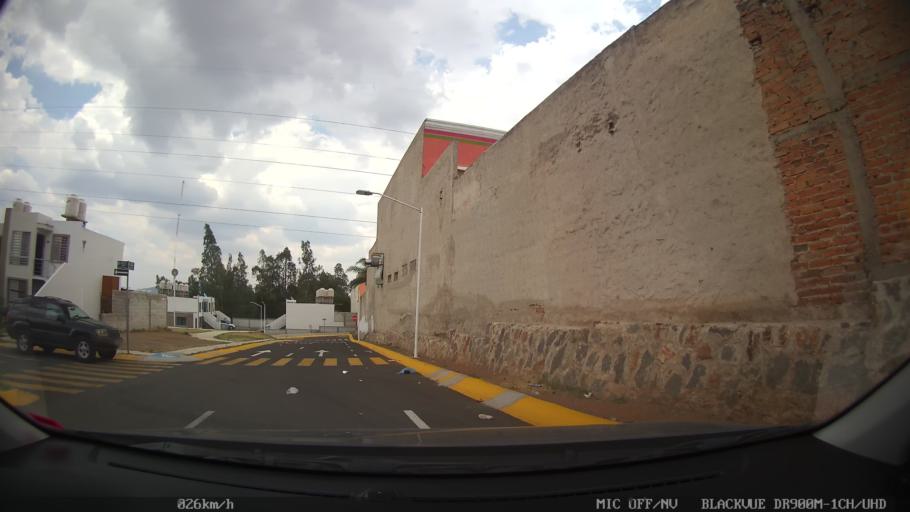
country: MX
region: Jalisco
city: Tonala
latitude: 20.6438
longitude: -103.2239
